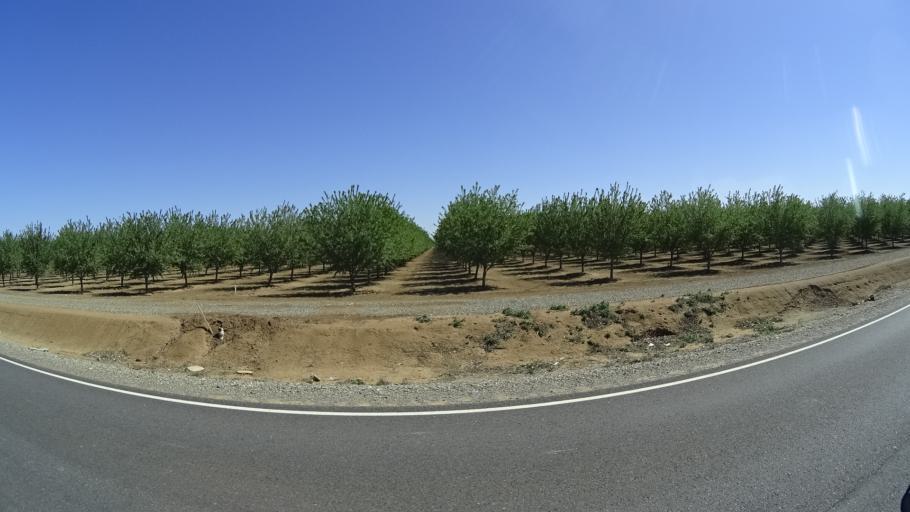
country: US
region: California
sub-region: Glenn County
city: Willows
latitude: 39.5493
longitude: -122.2494
